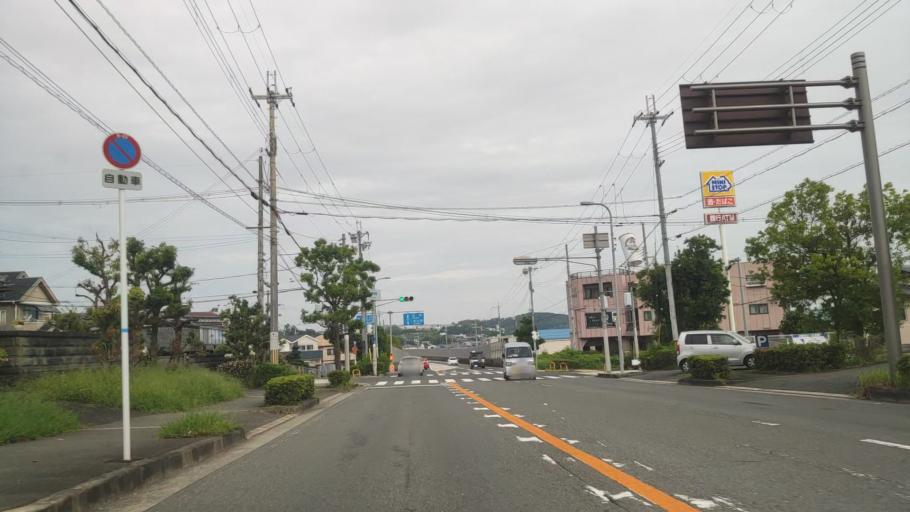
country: JP
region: Osaka
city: Tondabayashicho
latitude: 34.4284
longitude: 135.5700
